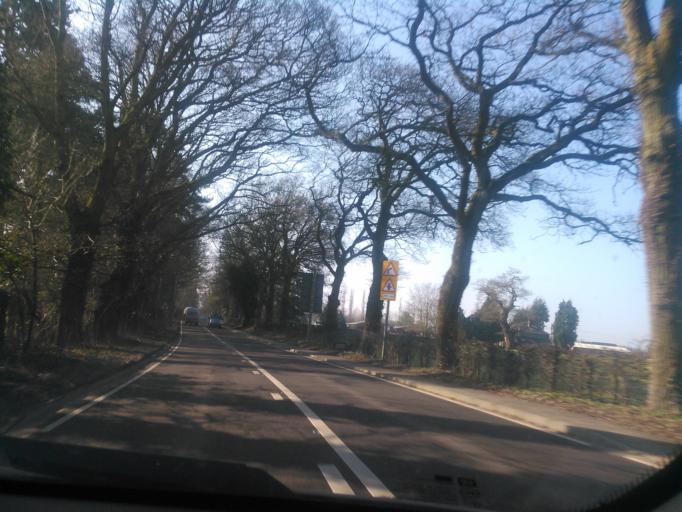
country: GB
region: England
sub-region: Shropshire
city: Craven Arms
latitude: 52.4563
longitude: -2.8371
